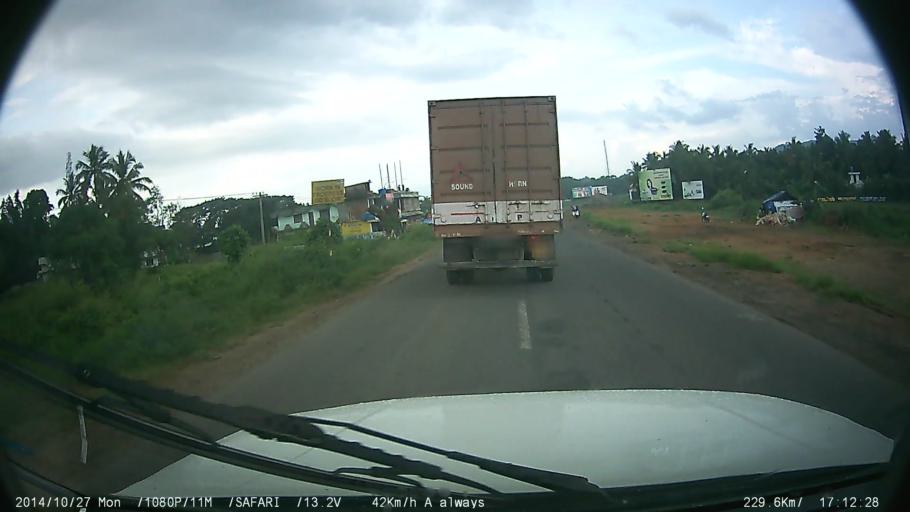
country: IN
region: Kerala
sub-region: Thrissur District
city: Chelakara
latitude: 10.6117
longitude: 76.4977
